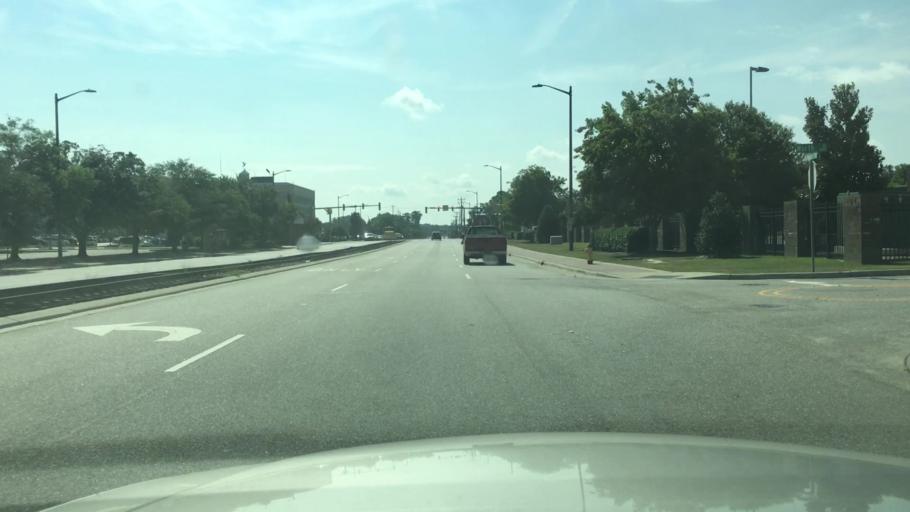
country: US
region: North Carolina
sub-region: Cumberland County
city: Fayetteville
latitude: 35.0511
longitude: -78.8808
